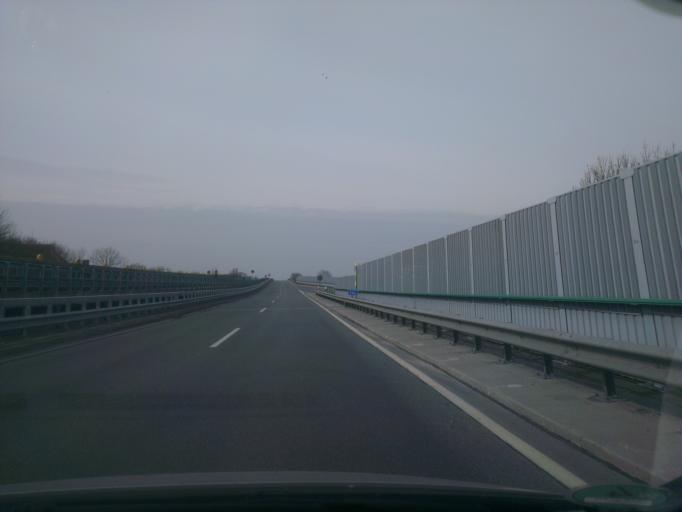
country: DE
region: Lower Saxony
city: Emden
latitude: 53.3881
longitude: 7.2057
